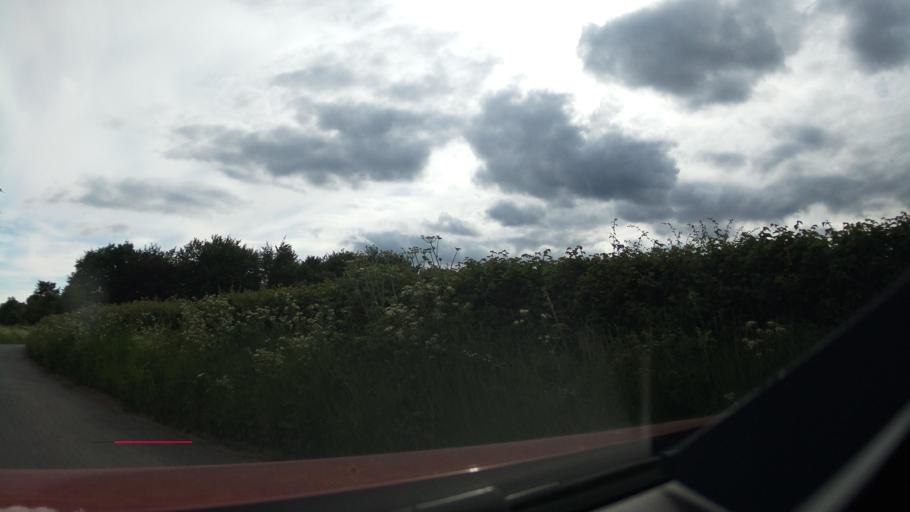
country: GB
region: England
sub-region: Gloucestershire
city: Moreton in Marsh
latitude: 52.0125
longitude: -1.7188
